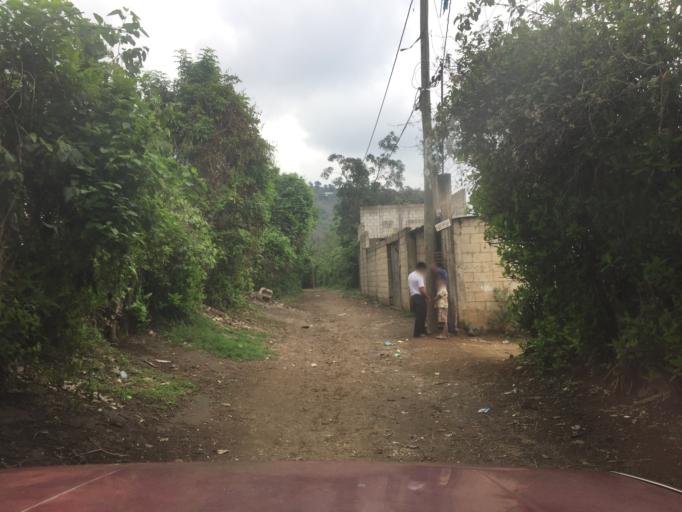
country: GT
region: Sacatepequez
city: Magdalena Milpas Altas
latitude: 14.5100
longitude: -90.6520
